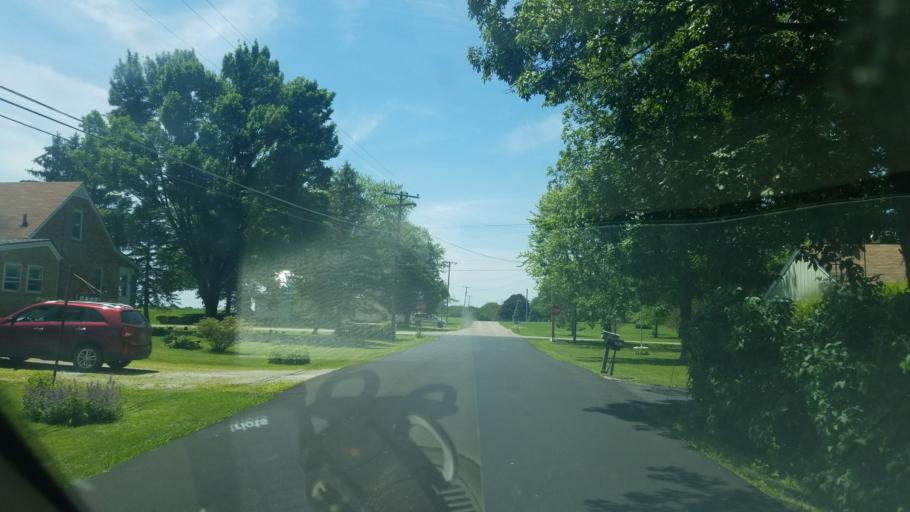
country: US
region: Ohio
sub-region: Stark County
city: Alliance
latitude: 40.8581
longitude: -81.1714
